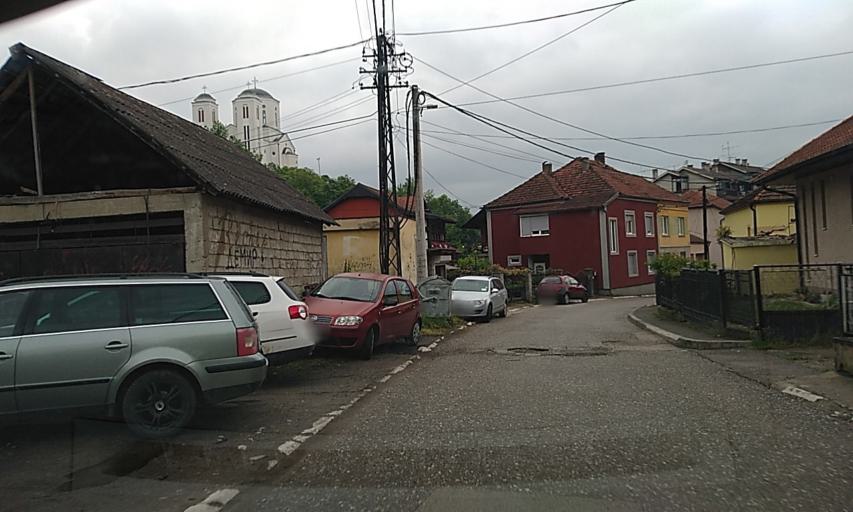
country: RS
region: Central Serbia
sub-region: Pcinjski Okrug
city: Vladicin Han
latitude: 42.7089
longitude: 22.0561
